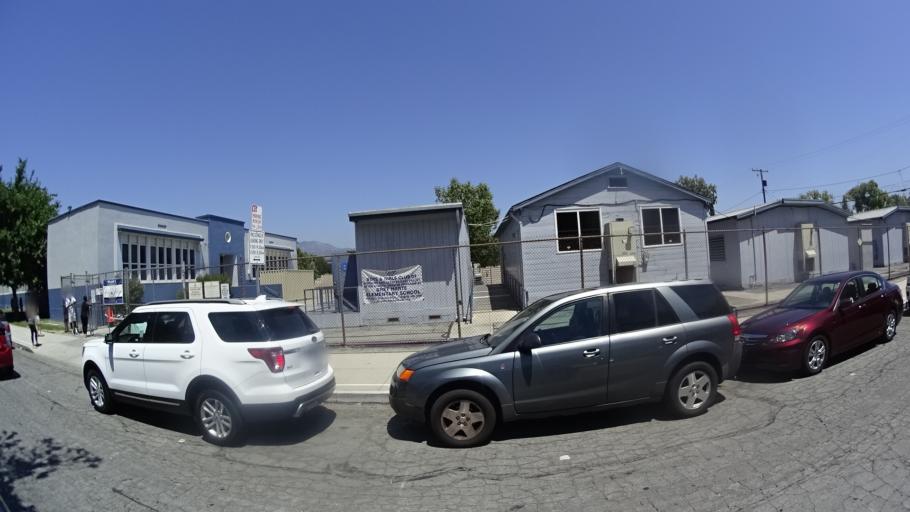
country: US
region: California
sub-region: Los Angeles County
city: North Hollywood
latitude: 34.1799
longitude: -118.3471
